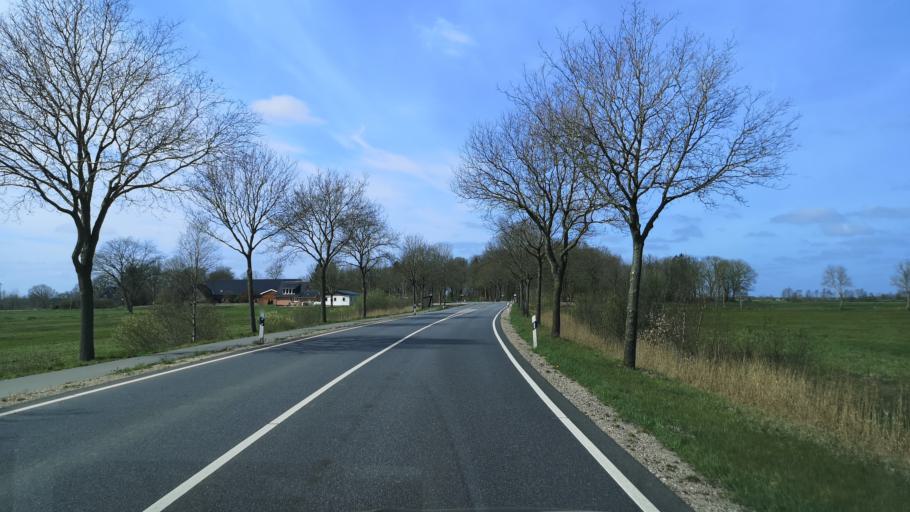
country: DE
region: Schleswig-Holstein
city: Prinzenmoor
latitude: 54.2222
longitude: 9.4586
